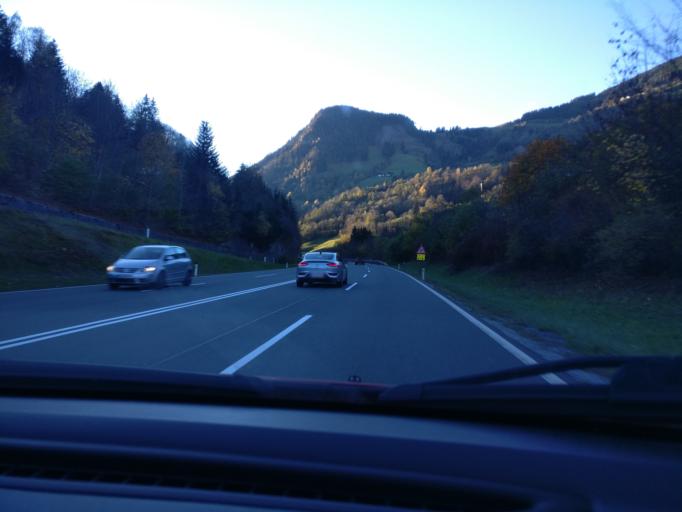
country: AT
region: Salzburg
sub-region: Politischer Bezirk Zell am See
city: Lend
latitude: 47.3063
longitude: 13.0248
